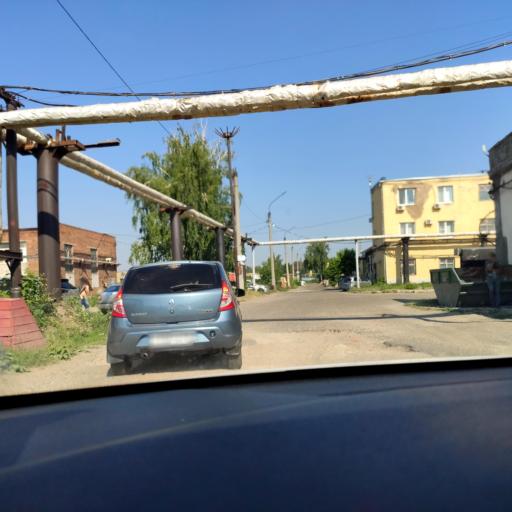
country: RU
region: Tatarstan
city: Verkhniy Uslon
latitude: 55.8013
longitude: 49.0421
